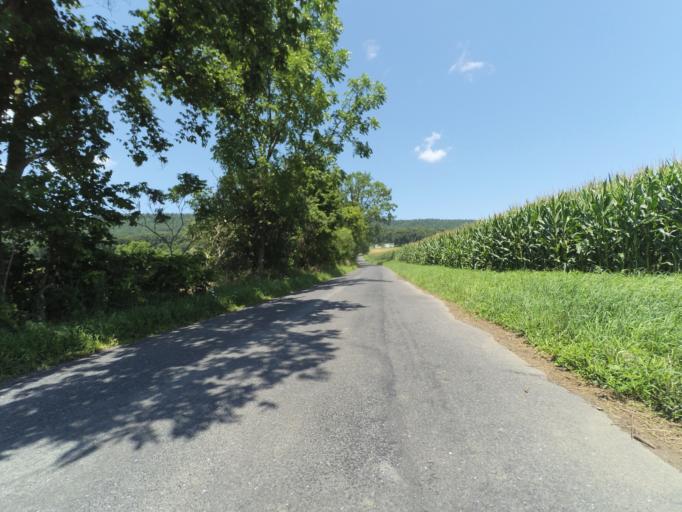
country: US
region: Pennsylvania
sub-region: Centre County
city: Boalsburg
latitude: 40.8028
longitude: -77.7665
